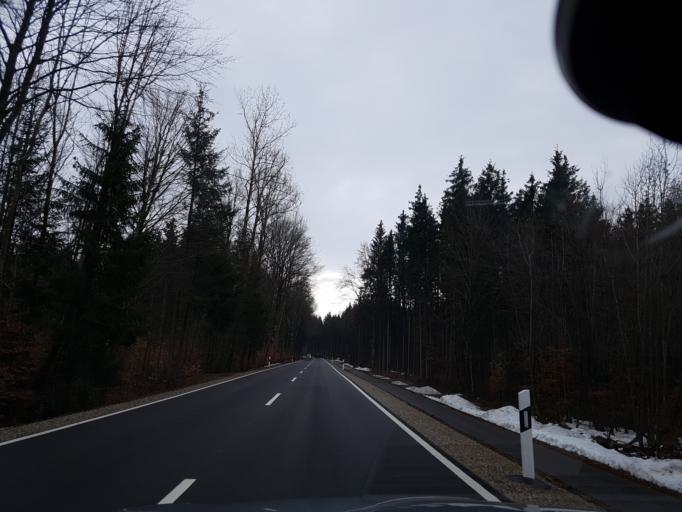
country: DE
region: Bavaria
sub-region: Upper Bavaria
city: Hohenkirchen-Siegertsbrunn
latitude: 48.0014
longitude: 11.7068
